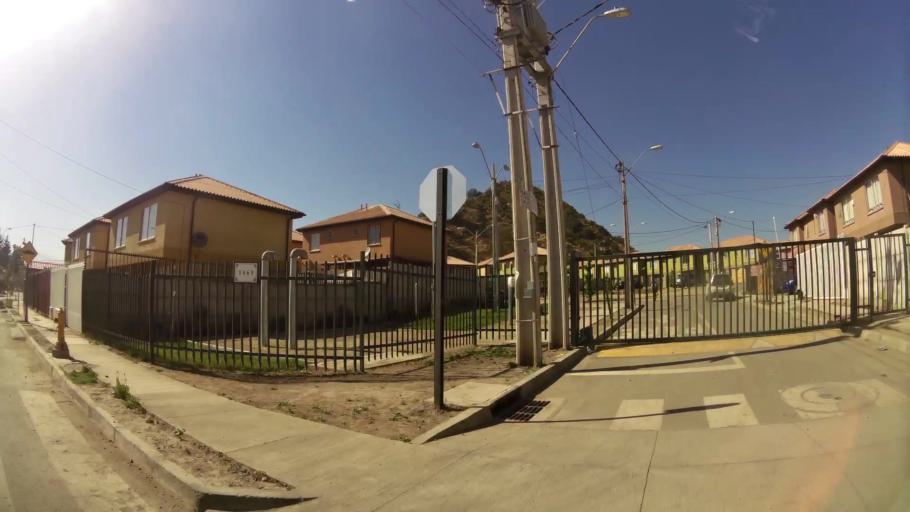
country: CL
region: Santiago Metropolitan
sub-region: Provincia de Maipo
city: San Bernardo
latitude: -33.6105
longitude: -70.6760
